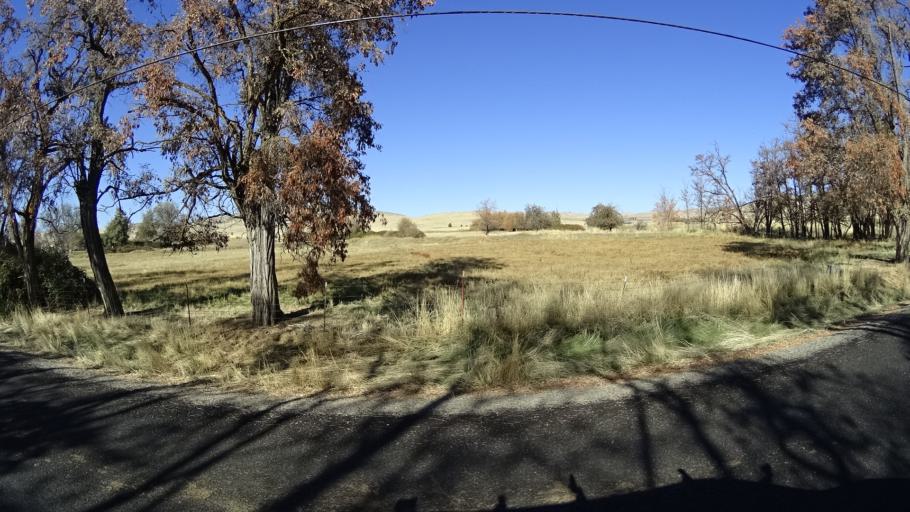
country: US
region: California
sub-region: Siskiyou County
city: Montague
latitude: 41.7262
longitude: -122.4091
